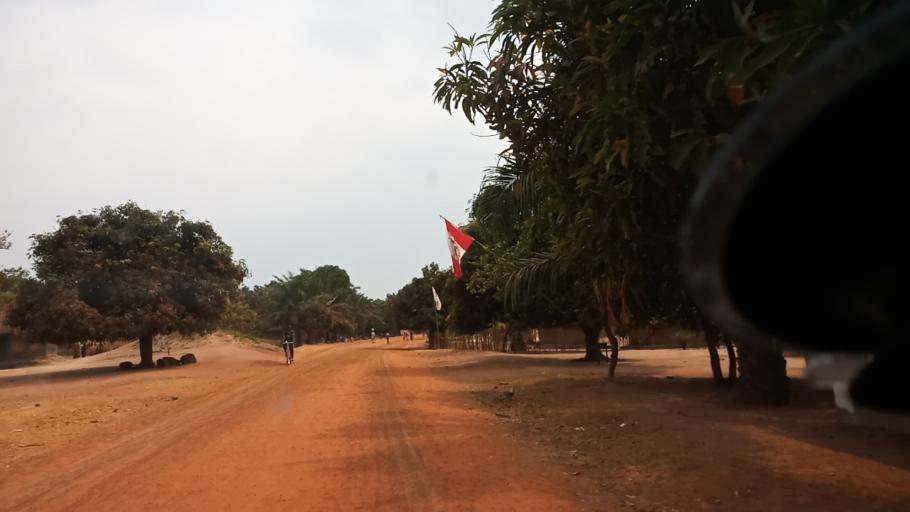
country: ZM
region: Luapula
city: Nchelenge
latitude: -9.1319
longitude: 28.2997
